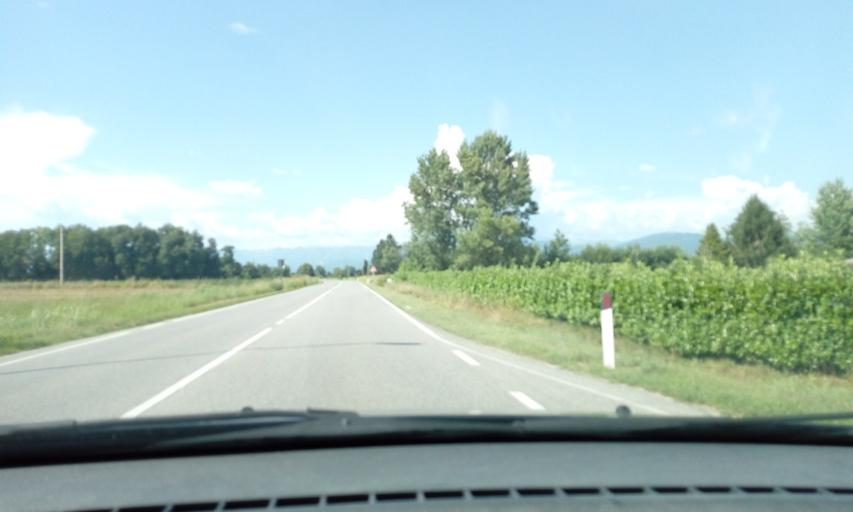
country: IT
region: Friuli Venezia Giulia
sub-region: Provincia di Udine
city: Pradamano
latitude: 46.0536
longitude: 13.3140
